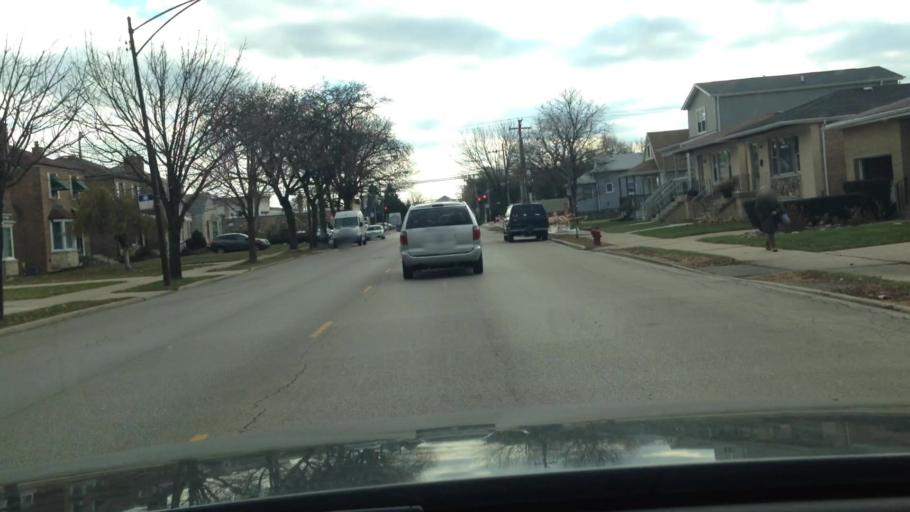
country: US
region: Illinois
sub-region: Cook County
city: Harwood Heights
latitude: 41.9698
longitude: -87.7880
